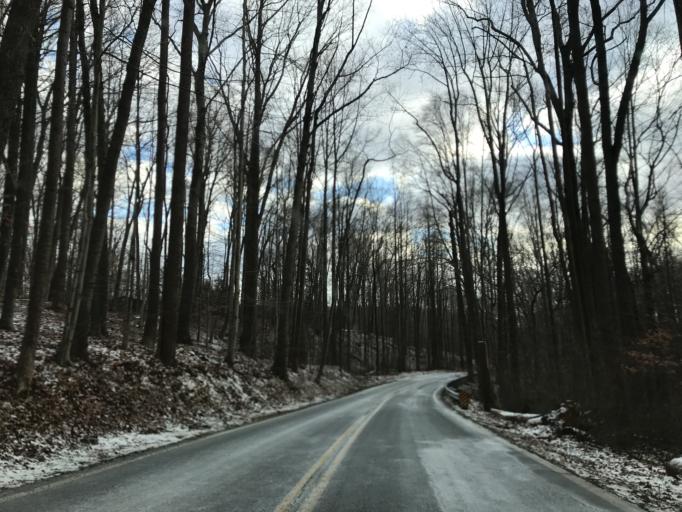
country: US
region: Maryland
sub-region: Harford County
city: Bel Air North
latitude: 39.6332
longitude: -76.3758
